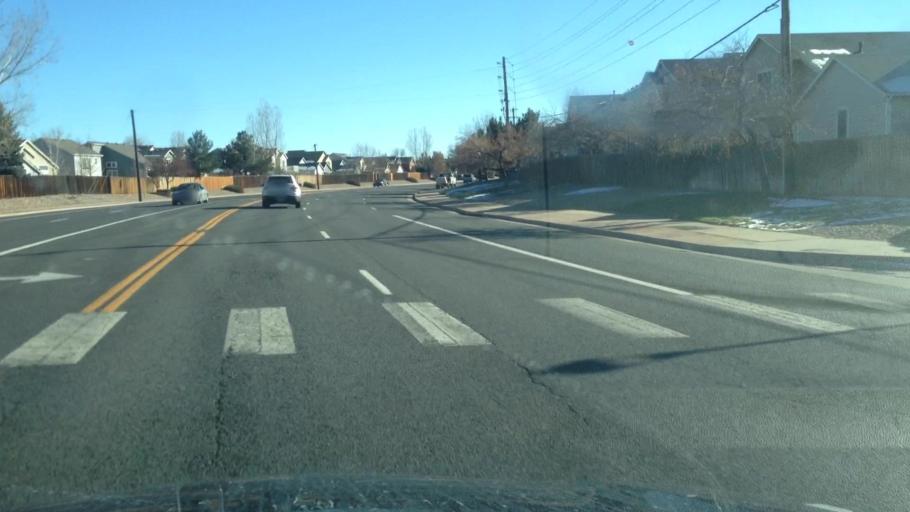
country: US
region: Colorado
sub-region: Douglas County
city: Stonegate
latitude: 39.5597
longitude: -104.7964
